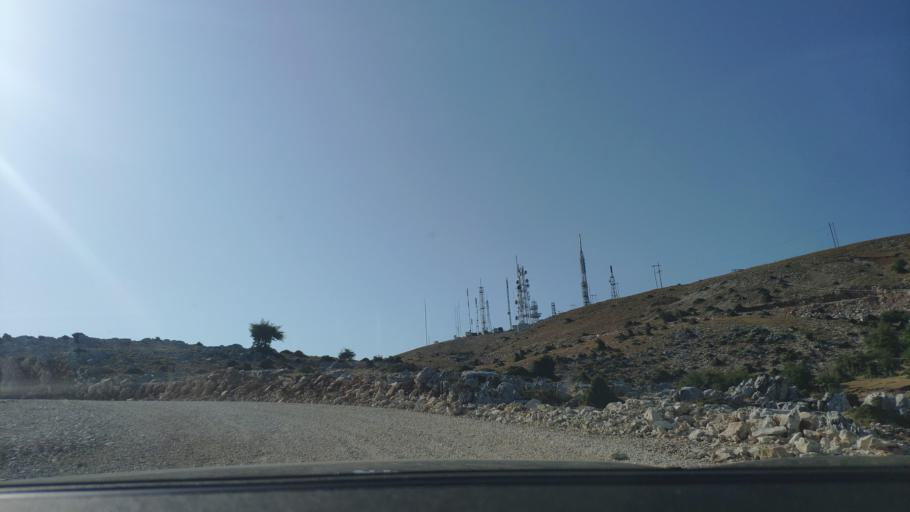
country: GR
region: West Greece
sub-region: Nomos Aitolias kai Akarnanias
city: Monastirakion
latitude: 38.8118
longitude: 20.9825
